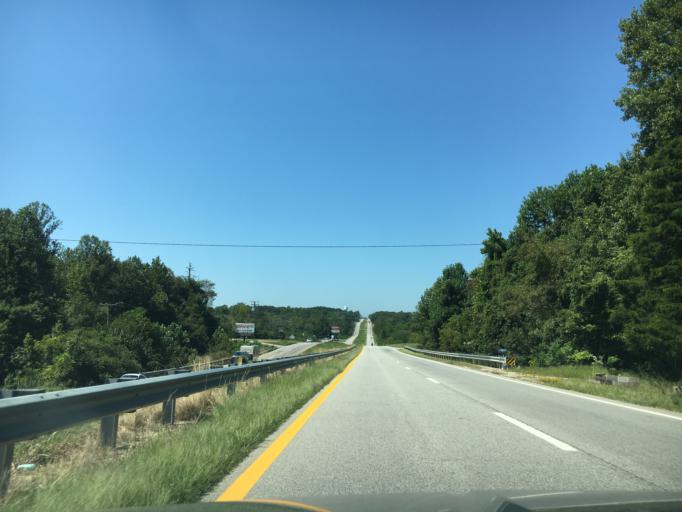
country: US
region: Virginia
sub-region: City of Danville
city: Danville
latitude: 36.5809
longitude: -79.2840
